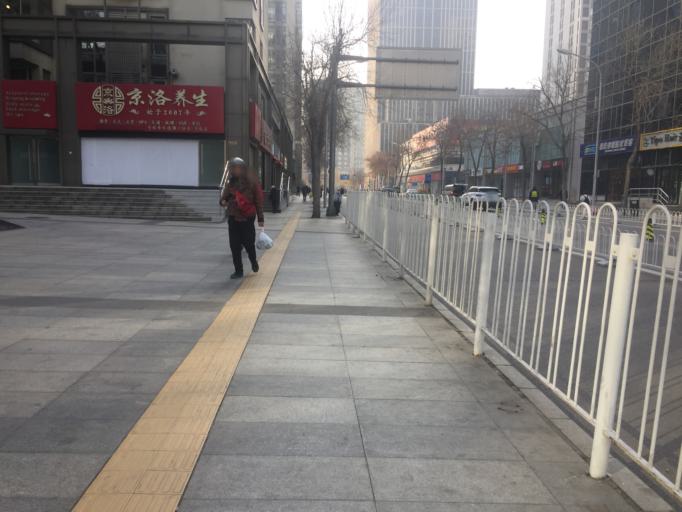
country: CN
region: Beijing
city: Chaowai
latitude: 39.9105
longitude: 116.4656
